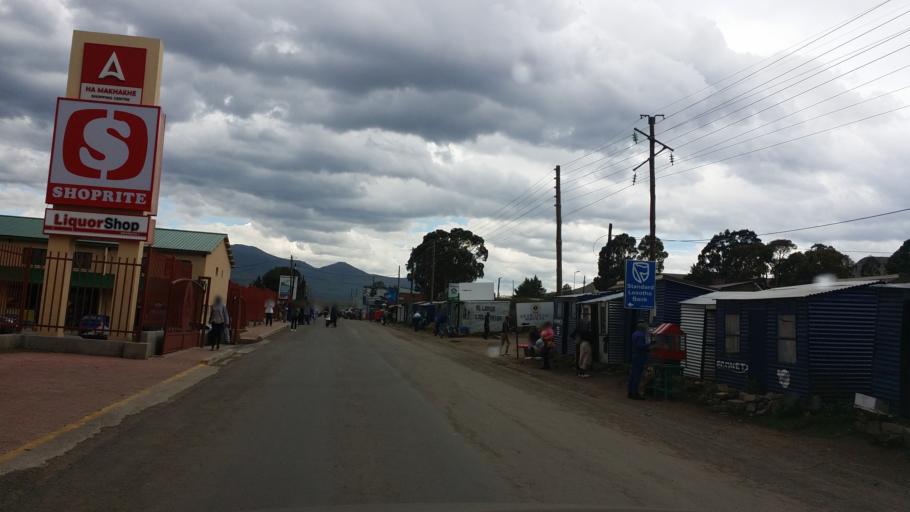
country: LS
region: Mokhotlong
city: Mokhotlong
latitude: -29.2887
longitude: 29.0640
